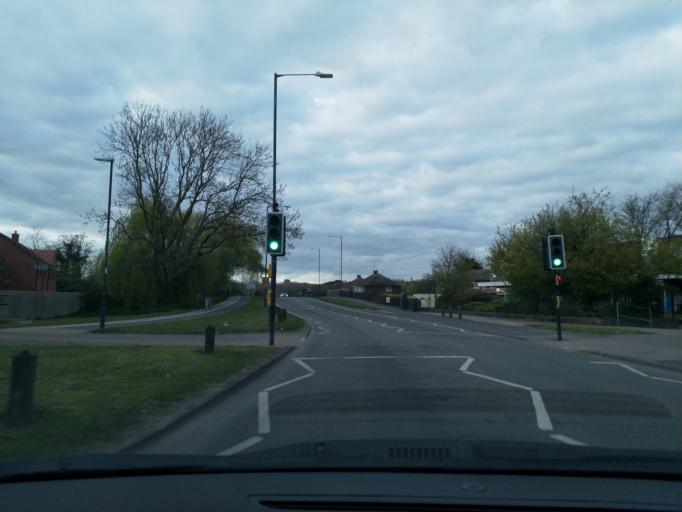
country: GB
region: England
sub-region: Warwickshire
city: Royal Leamington Spa
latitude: 52.2825
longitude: -1.5173
